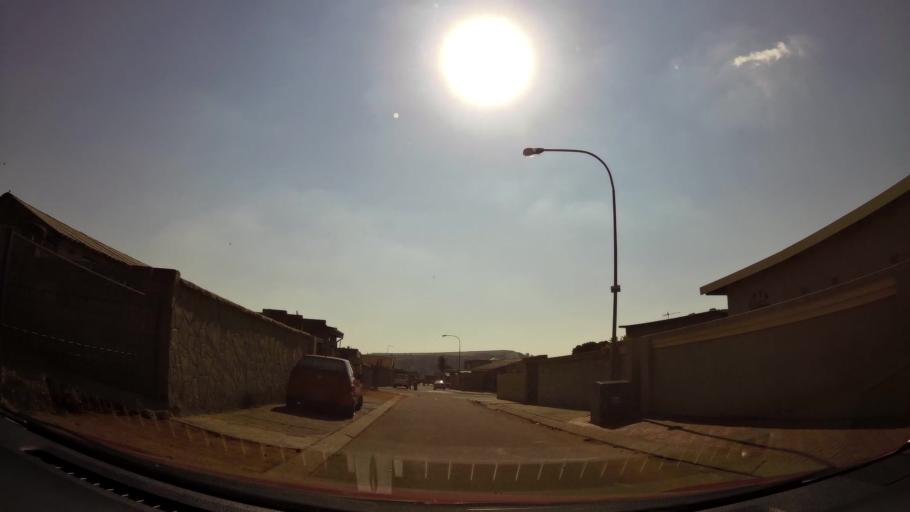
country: ZA
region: Gauteng
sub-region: City of Johannesburg Metropolitan Municipality
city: Johannesburg
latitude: -26.2417
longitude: 27.9603
